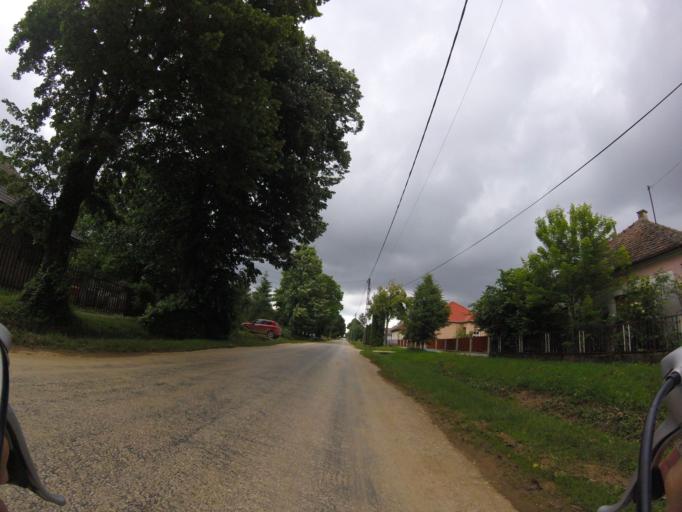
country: HU
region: Baranya
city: Pellerd
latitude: 45.9696
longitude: 18.1380
